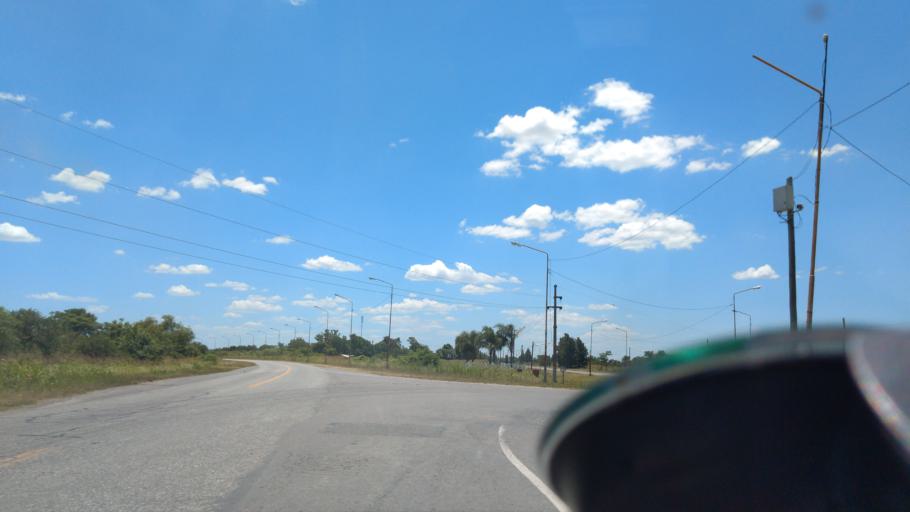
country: AR
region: Santa Fe
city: Laguna Paiva
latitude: -31.3274
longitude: -60.6595
